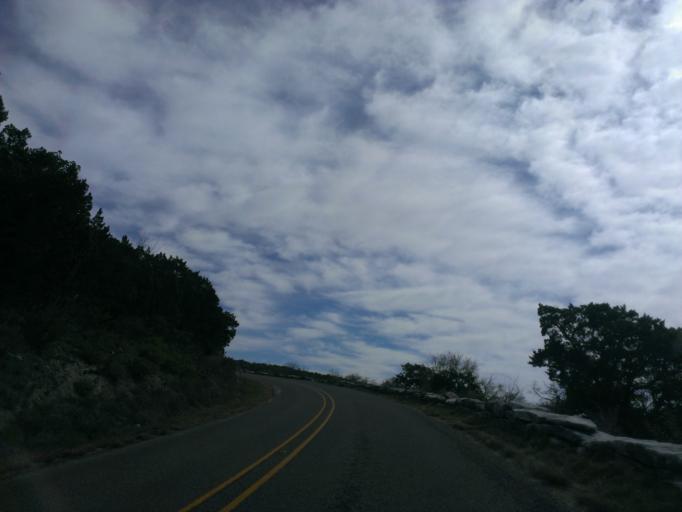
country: US
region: Texas
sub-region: Llano County
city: Buchanan Dam
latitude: 30.6975
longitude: -98.3803
